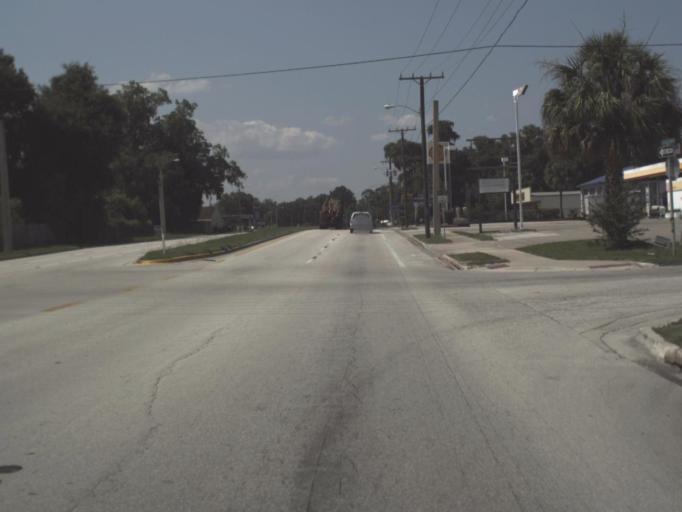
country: US
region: Florida
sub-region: Alachua County
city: Hawthorne
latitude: 29.5885
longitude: -82.0846
